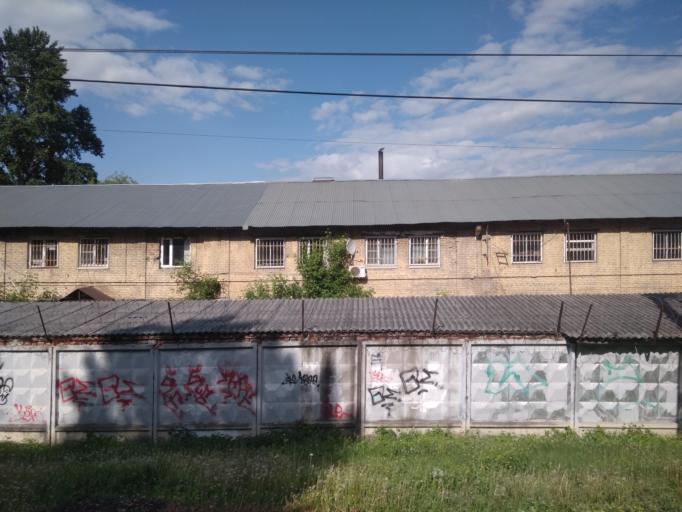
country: RU
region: Moscow
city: Mar'ina Roshcha
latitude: 55.8033
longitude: 37.5999
